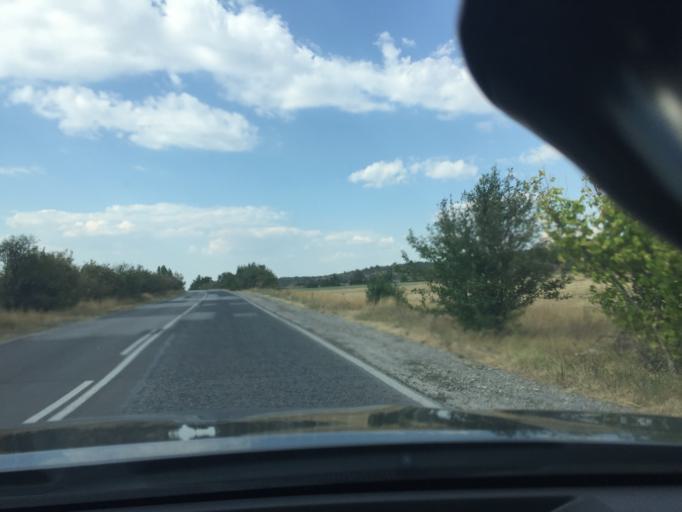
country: BG
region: Kyustendil
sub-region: Obshtina Boboshevo
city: Boboshevo
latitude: 42.1267
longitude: 23.0396
